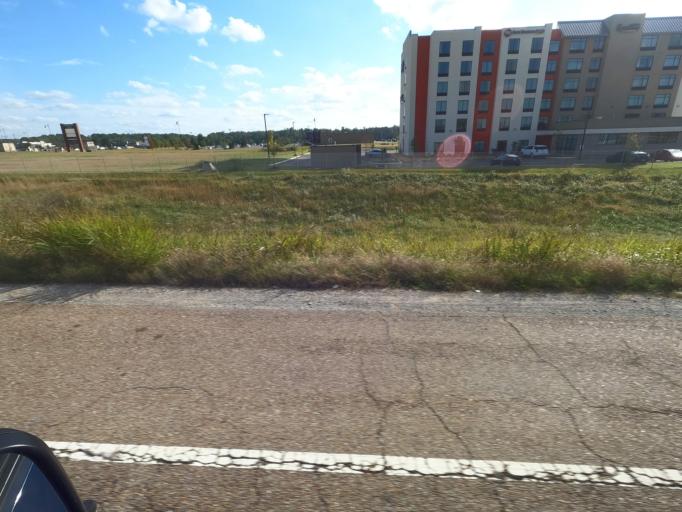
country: US
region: Tennessee
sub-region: Madison County
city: Jackson
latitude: 35.6778
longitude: -88.7840
